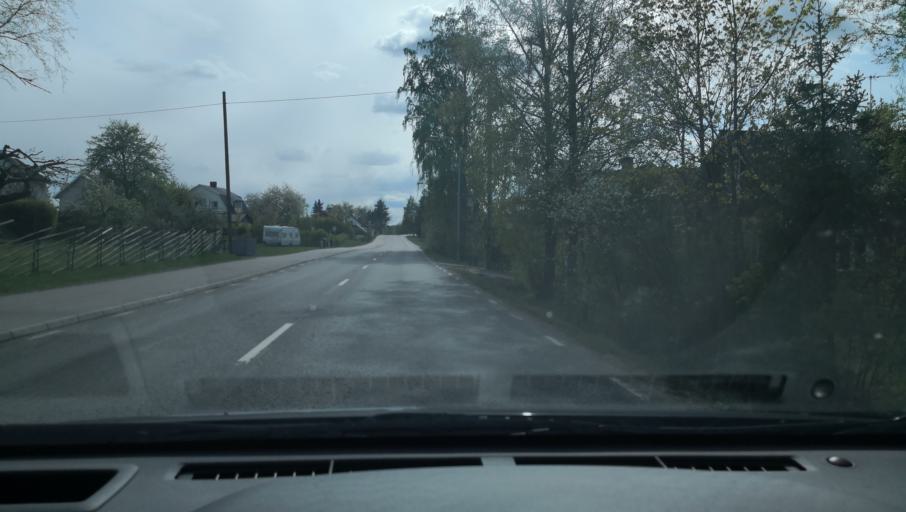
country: SE
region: OErebro
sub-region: Hallsbergs Kommun
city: Hallsberg
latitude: 59.0744
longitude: 15.1407
